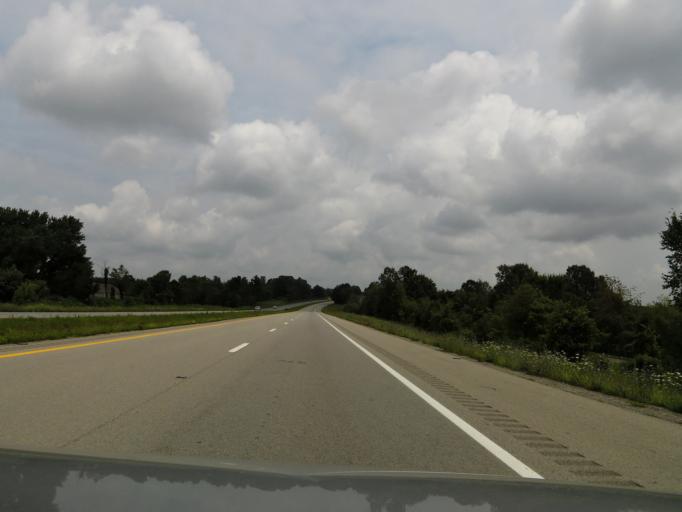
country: US
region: Kentucky
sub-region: Grayson County
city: Leitchfield
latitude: 37.5211
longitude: -86.1478
